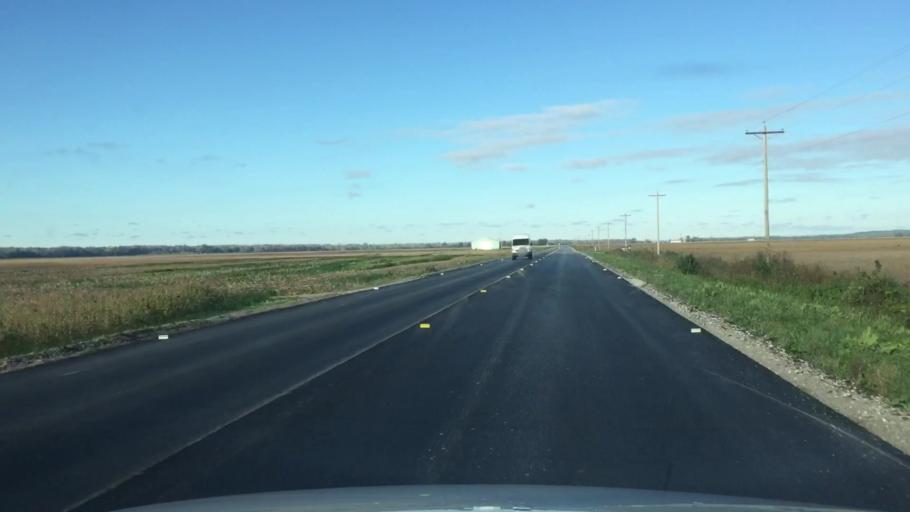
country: US
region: Missouri
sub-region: Howard County
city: New Franklin
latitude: 38.9917
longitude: -92.6268
